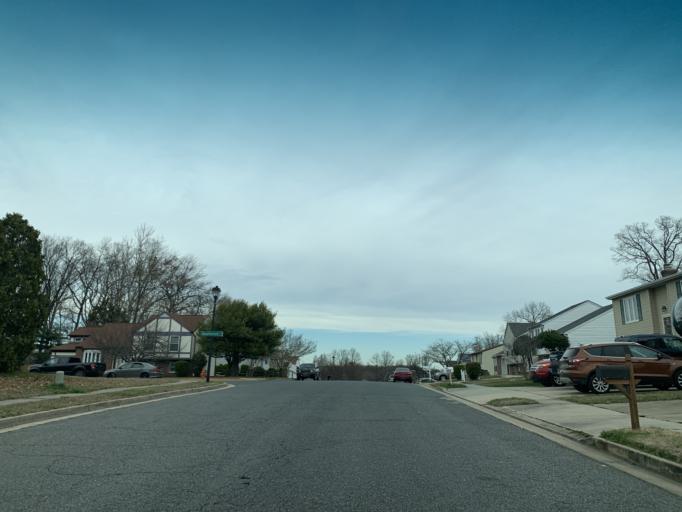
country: US
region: Maryland
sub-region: Baltimore County
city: Rossville
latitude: 39.3349
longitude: -76.4620
